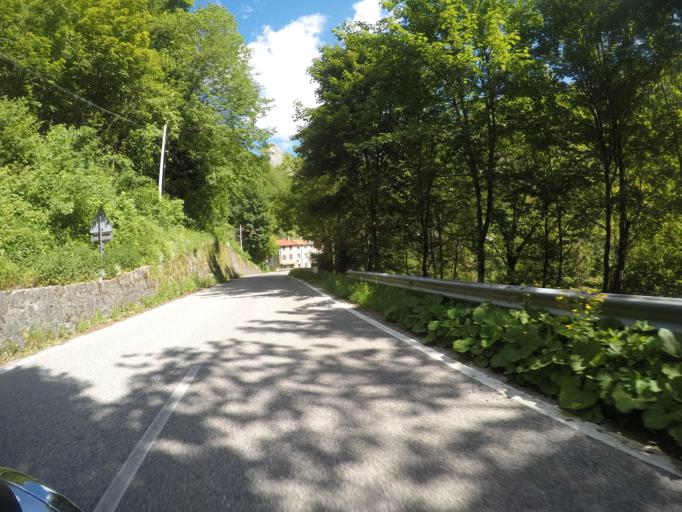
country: IT
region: Tuscany
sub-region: Provincia di Lucca
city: Fontana delle Monache
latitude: 44.0632
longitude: 10.2491
